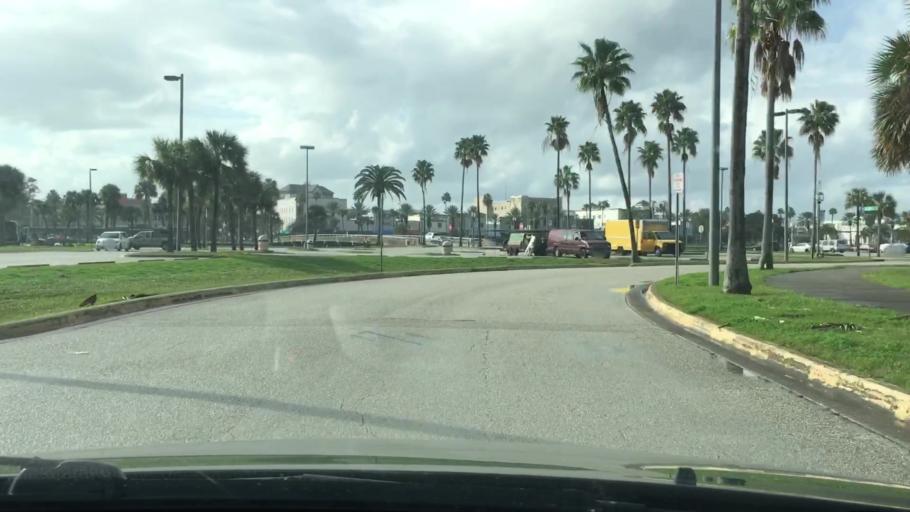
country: US
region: Florida
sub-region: Volusia County
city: Daytona Beach
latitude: 29.2109
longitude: -81.0157
